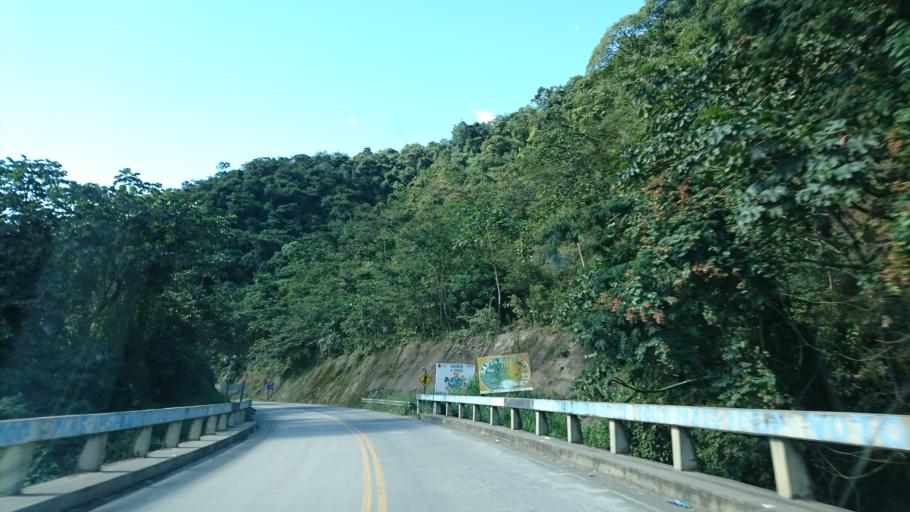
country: BO
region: La Paz
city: Coroico
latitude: -16.1948
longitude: -67.7430
